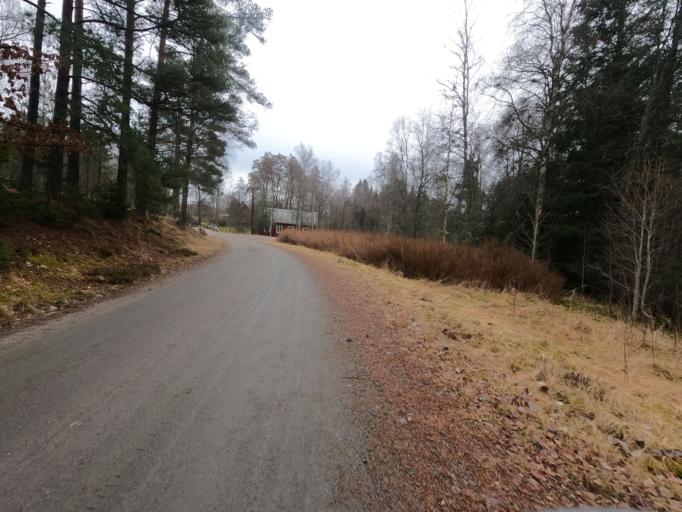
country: SE
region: Kronoberg
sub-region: Markaryds Kommun
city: Stromsnasbruk
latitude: 56.7879
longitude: 13.5602
